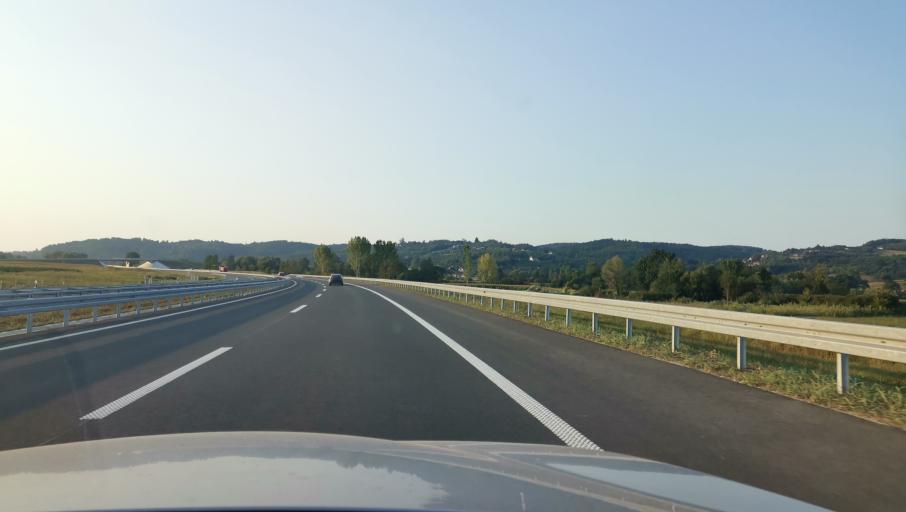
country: RS
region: Central Serbia
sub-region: Kolubarski Okrug
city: Lajkovac
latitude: 44.3261
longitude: 20.2128
